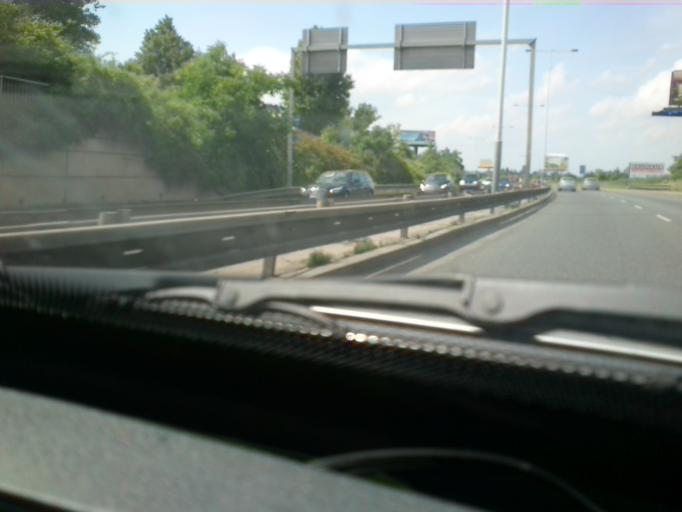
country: CZ
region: Praha
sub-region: Praha 9
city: Vysocany
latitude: 50.1203
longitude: 14.5168
